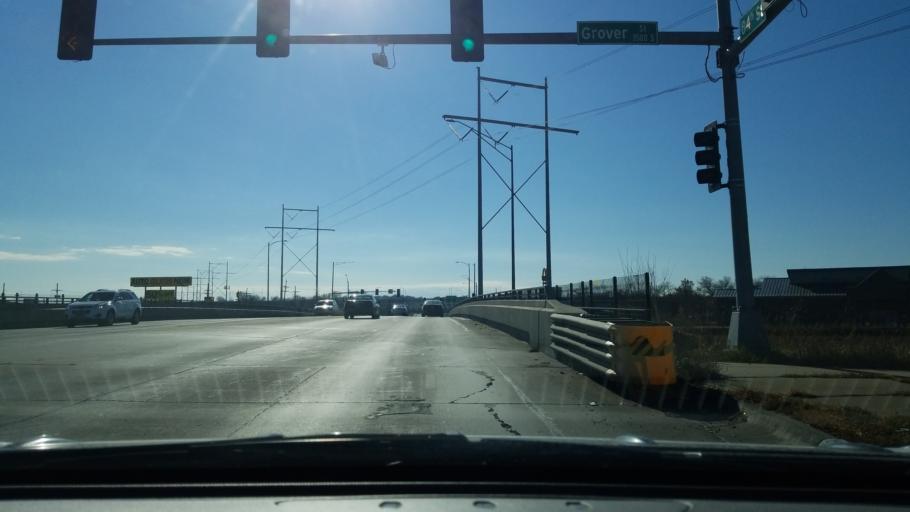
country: US
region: Nebraska
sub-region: Douglas County
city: Ralston
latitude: 41.2276
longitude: -96.0433
